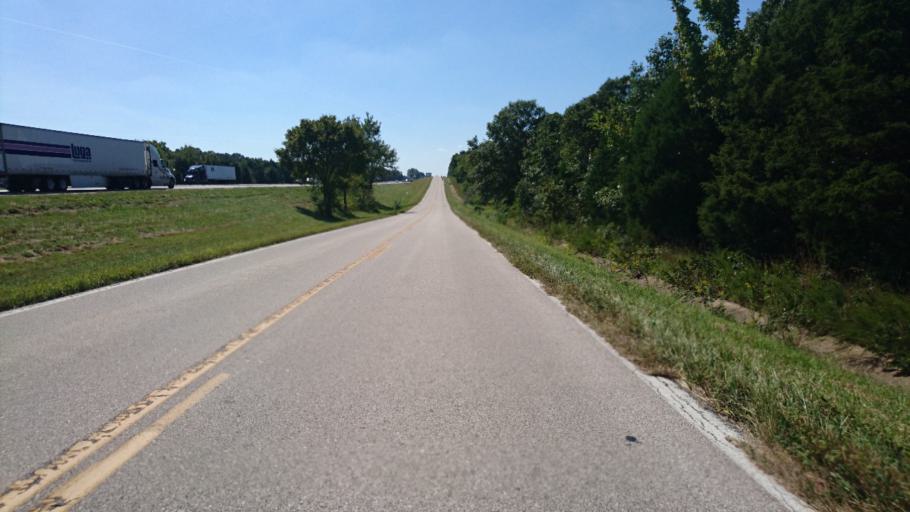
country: US
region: Missouri
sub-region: Franklin County
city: Sullivan
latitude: 38.2609
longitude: -91.1187
